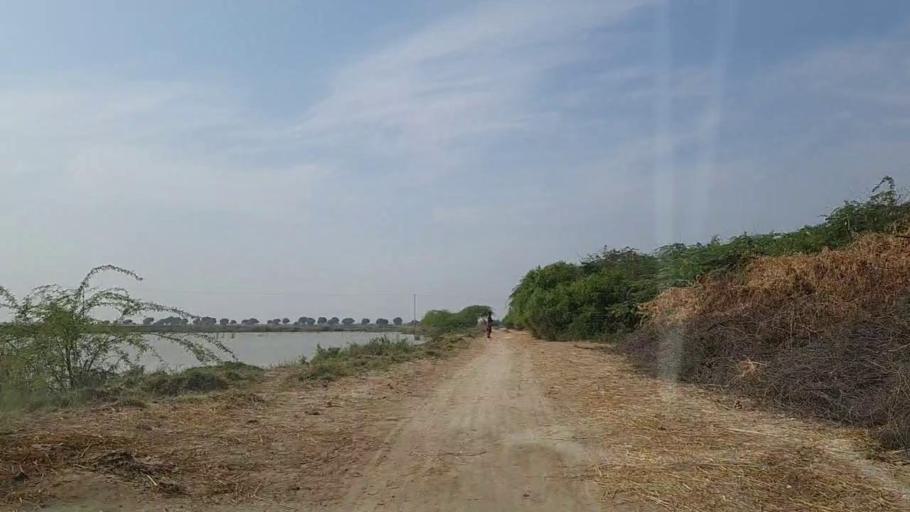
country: PK
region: Sindh
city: Mirpur Batoro
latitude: 24.6086
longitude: 68.2113
